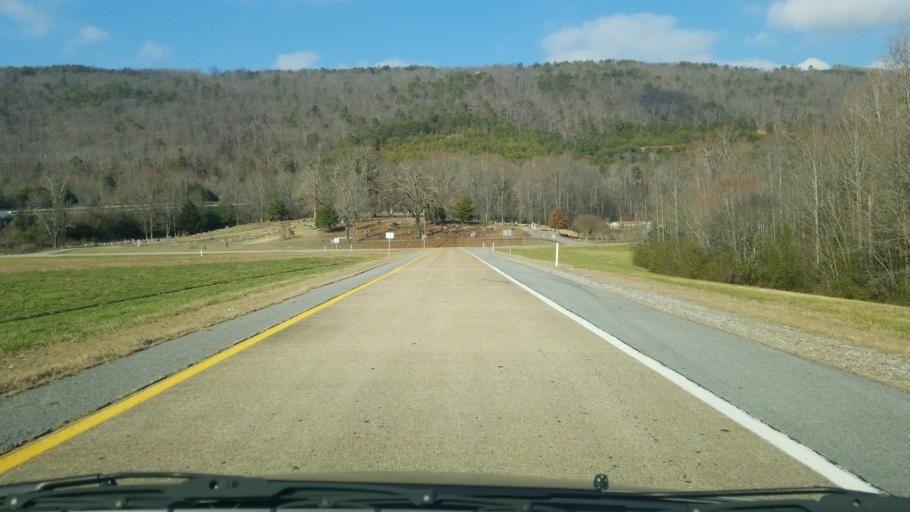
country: US
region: Tennessee
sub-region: Hamilton County
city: Soddy-Daisy
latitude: 35.3046
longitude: -85.1600
